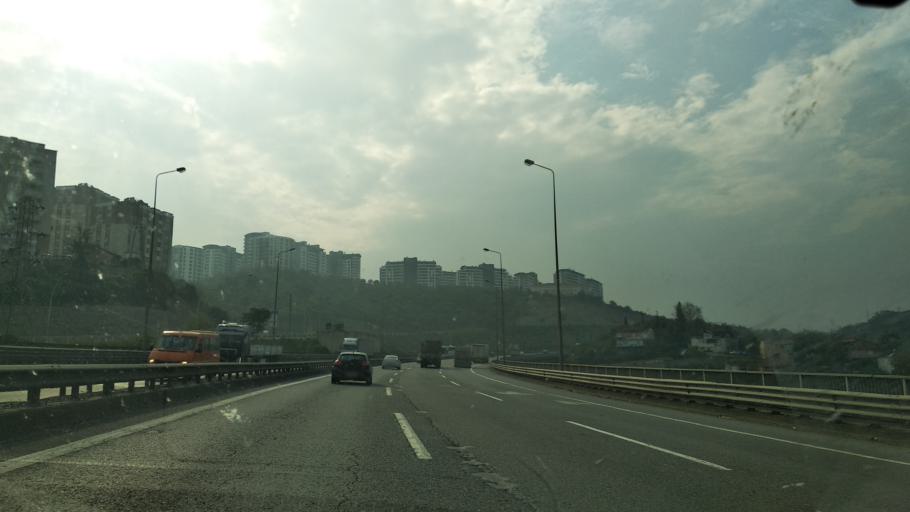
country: TR
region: Kocaeli
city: Izmit
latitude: 40.7834
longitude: 29.9426
